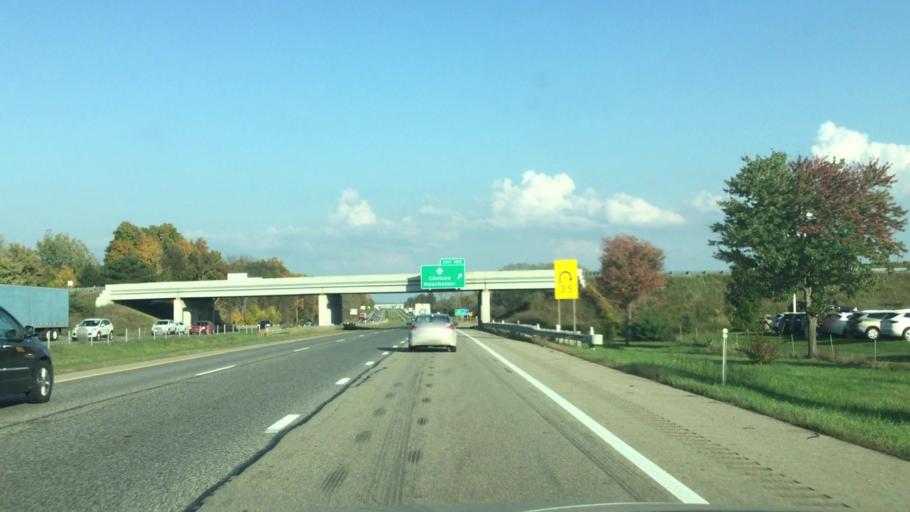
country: US
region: Michigan
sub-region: Washtenaw County
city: Chelsea
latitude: 42.2944
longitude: -84.0285
